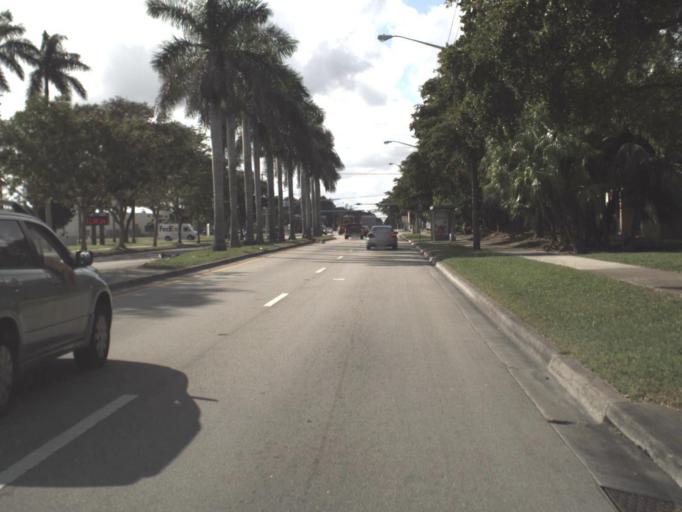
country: US
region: Florida
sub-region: Miami-Dade County
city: Leisure City
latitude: 25.4995
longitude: -80.4431
